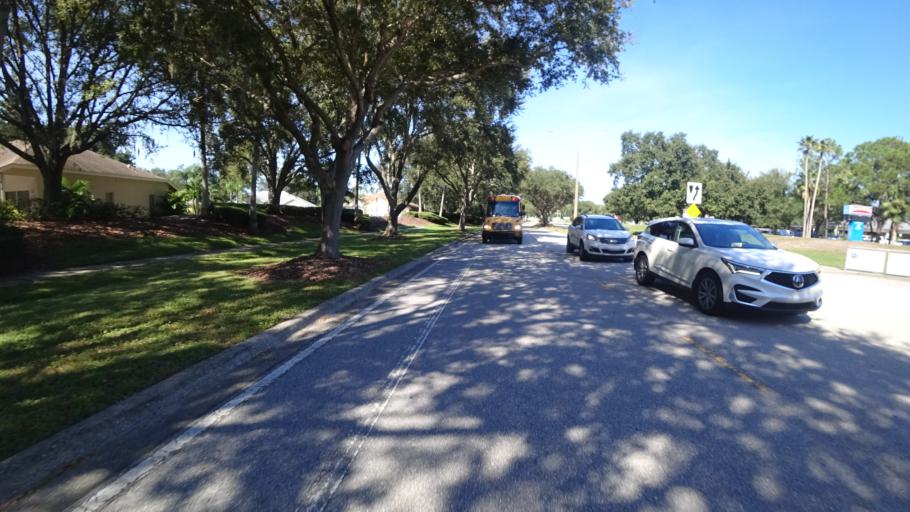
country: US
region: Florida
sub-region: Sarasota County
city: The Meadows
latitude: 27.4310
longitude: -82.4363
